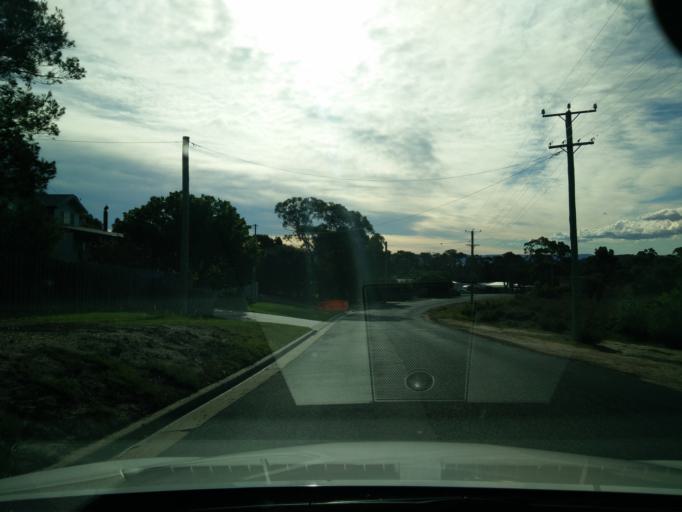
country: AU
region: Tasmania
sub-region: Break O'Day
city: St Helens
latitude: -42.1215
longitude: 148.2875
